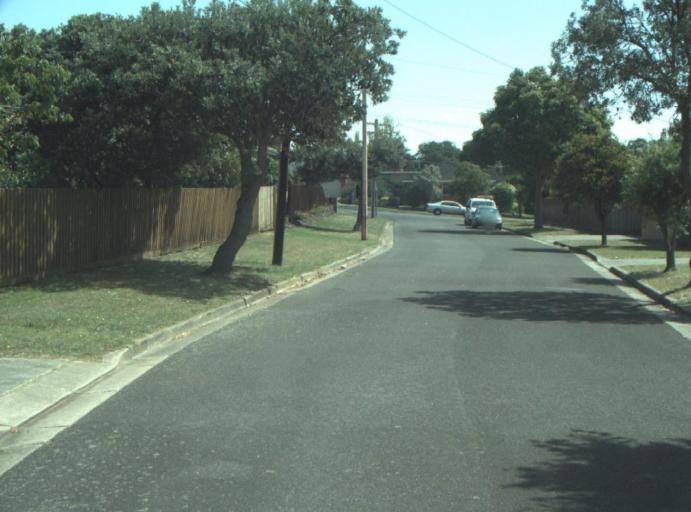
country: AU
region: Victoria
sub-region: Greater Geelong
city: Wandana Heights
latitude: -38.1690
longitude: 144.3220
